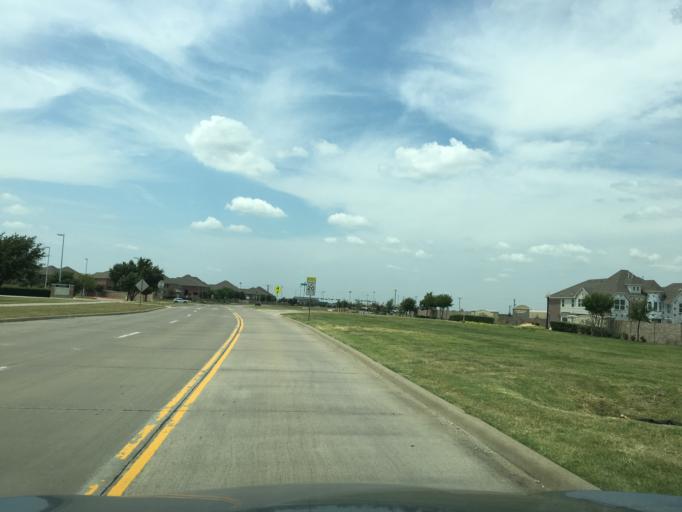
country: US
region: Texas
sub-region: Denton County
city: The Colony
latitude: 33.0352
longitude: -96.9198
